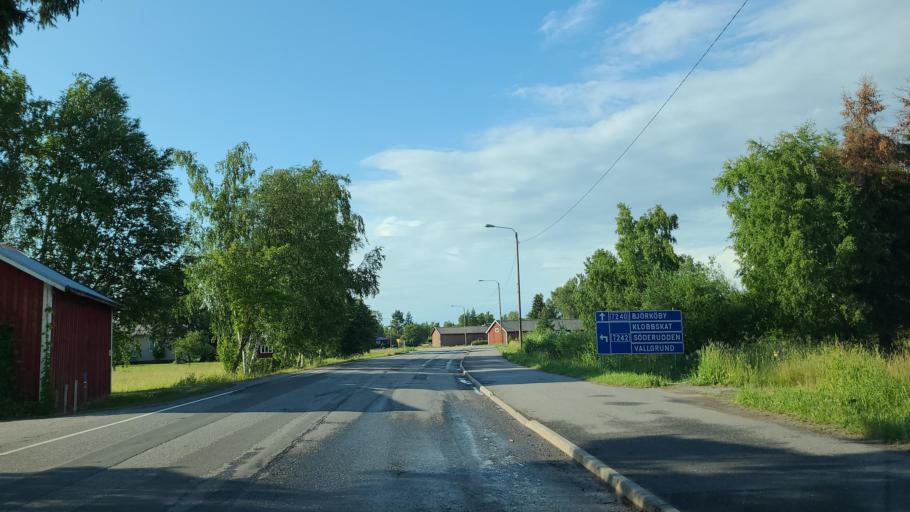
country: FI
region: Ostrobothnia
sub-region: Vaasa
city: Replot
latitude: 63.2291
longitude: 21.4104
